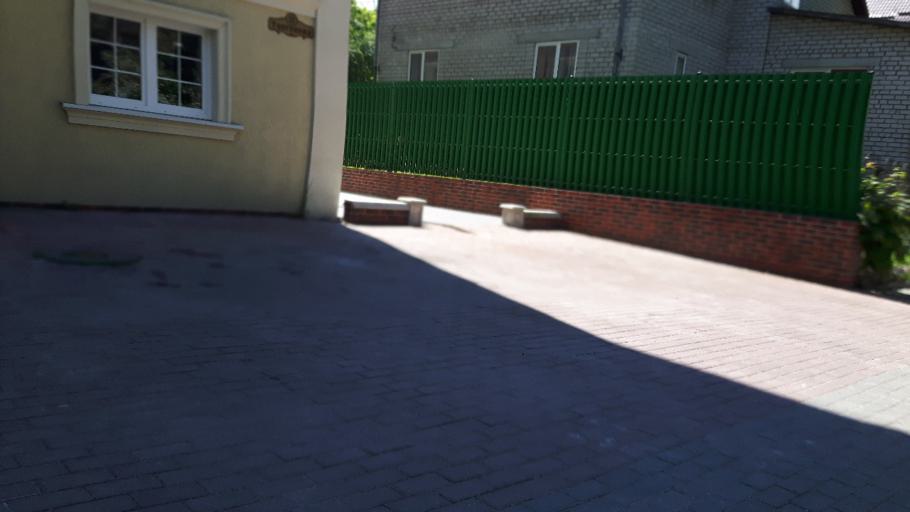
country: RU
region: Kaliningrad
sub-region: Gorod Kaliningrad
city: Kaliningrad
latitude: 54.7335
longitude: 20.5172
